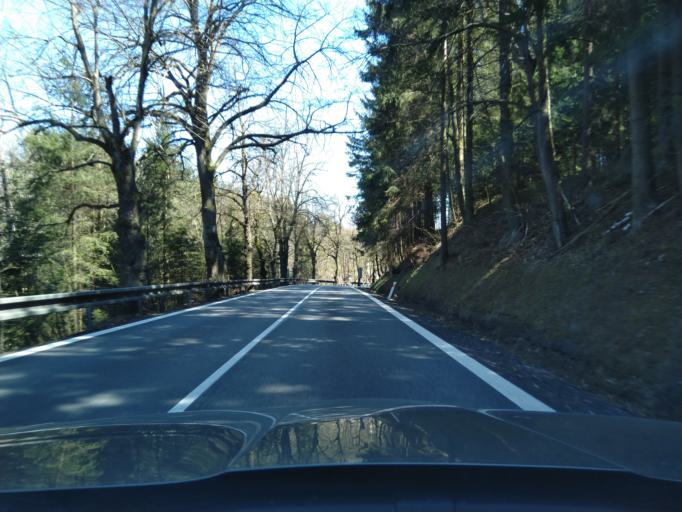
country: CZ
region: Jihocesky
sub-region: Okres Prachatice
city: Vimperk
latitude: 49.0492
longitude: 13.7647
